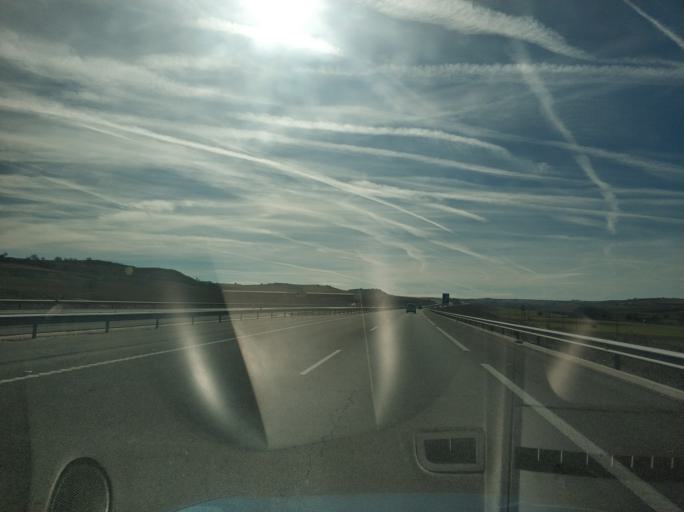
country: ES
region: Castille and Leon
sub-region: Provincia de Zamora
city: Corrales
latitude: 41.3460
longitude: -5.7172
